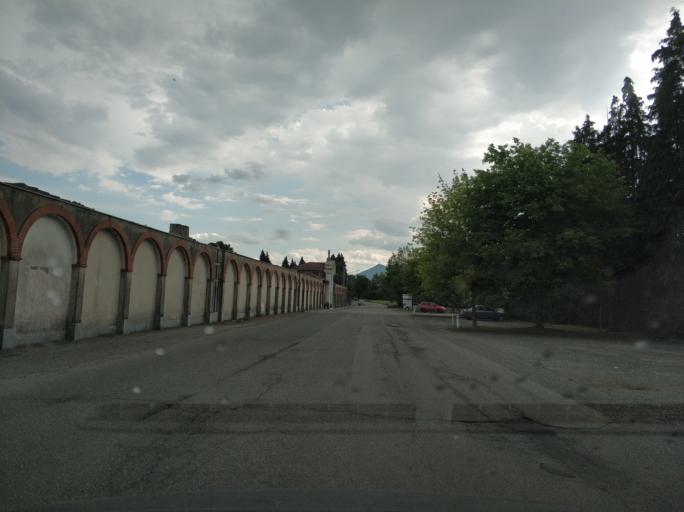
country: IT
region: Piedmont
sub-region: Provincia di Torino
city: Mathi
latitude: 45.2646
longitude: 7.5474
